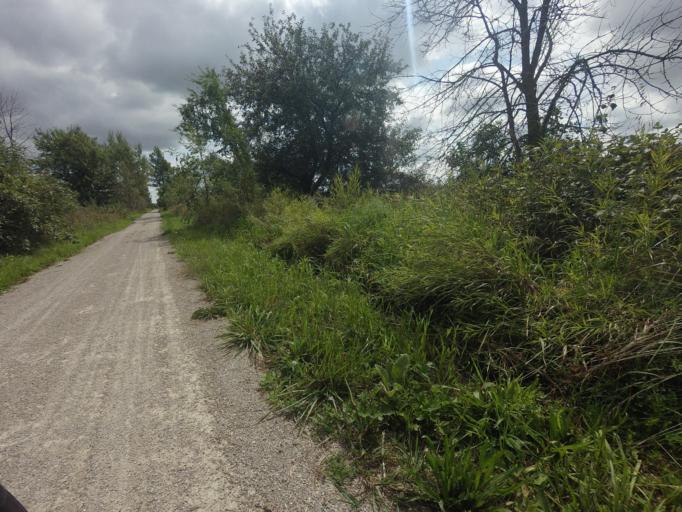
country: CA
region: Ontario
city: North Perth
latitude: 43.5796
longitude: -81.0564
